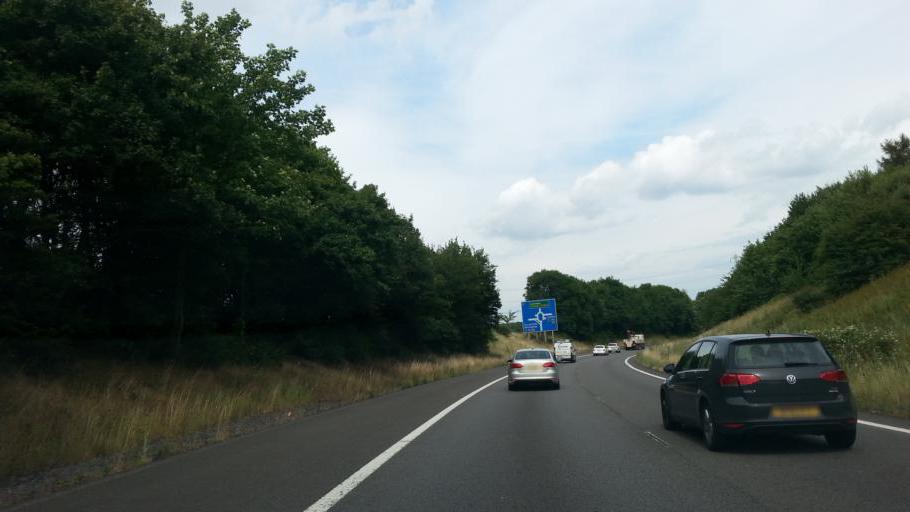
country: GB
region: England
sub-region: Leicestershire
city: Enderby
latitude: 52.6000
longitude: -1.2098
